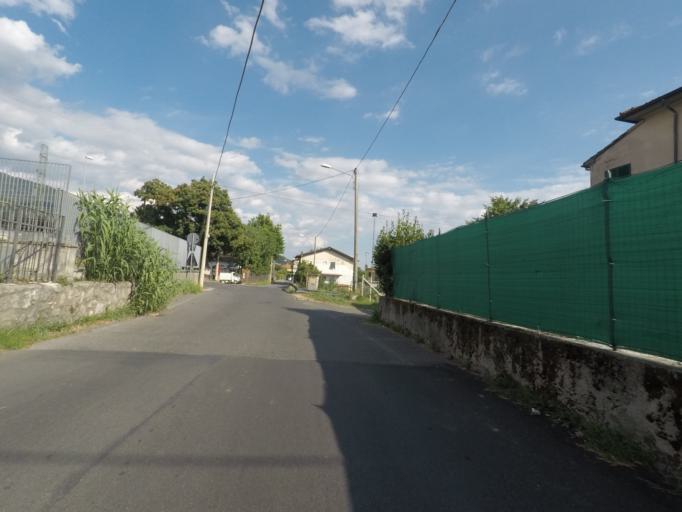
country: IT
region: Tuscany
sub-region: Provincia di Massa-Carrara
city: Massa
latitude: 44.0216
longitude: 10.1411
